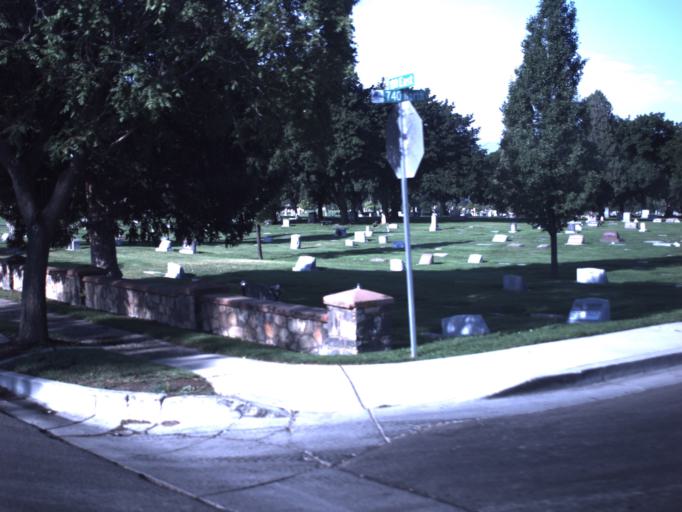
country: US
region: Utah
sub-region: Utah County
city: American Fork
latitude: 40.3917
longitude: -111.7958
